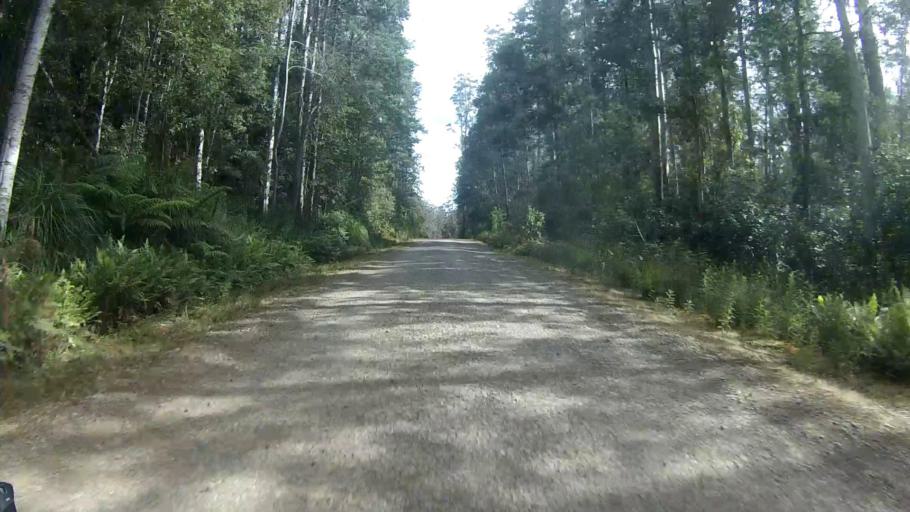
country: AU
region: Tasmania
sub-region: Sorell
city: Sorell
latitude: -42.7229
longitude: 147.8399
